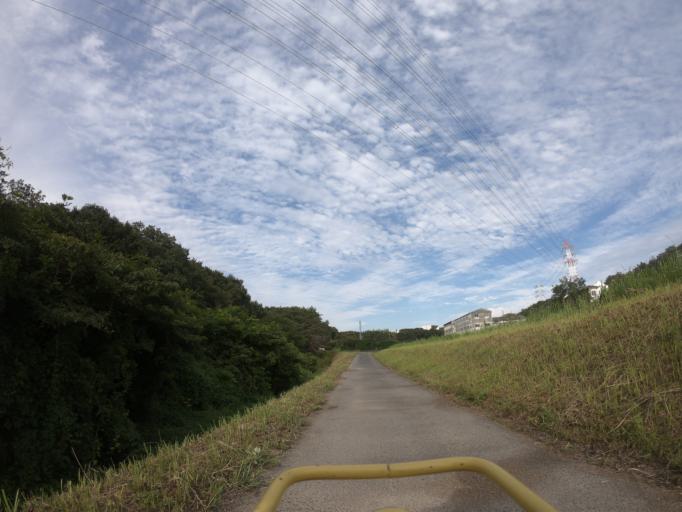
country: JP
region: Aichi
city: Seto
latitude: 35.1466
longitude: 137.0877
